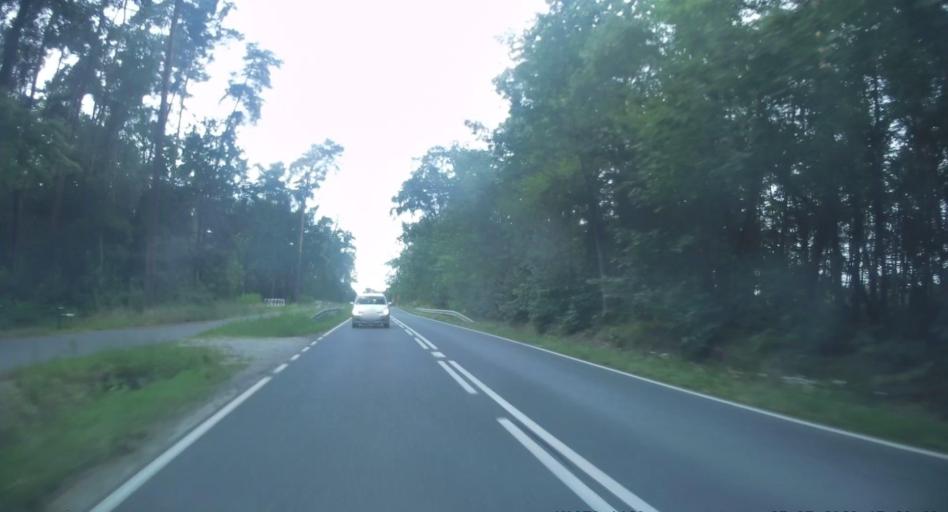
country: PL
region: Lesser Poland Voivodeship
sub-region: Powiat brzeski
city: Przyborow
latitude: 50.0549
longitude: 20.6392
